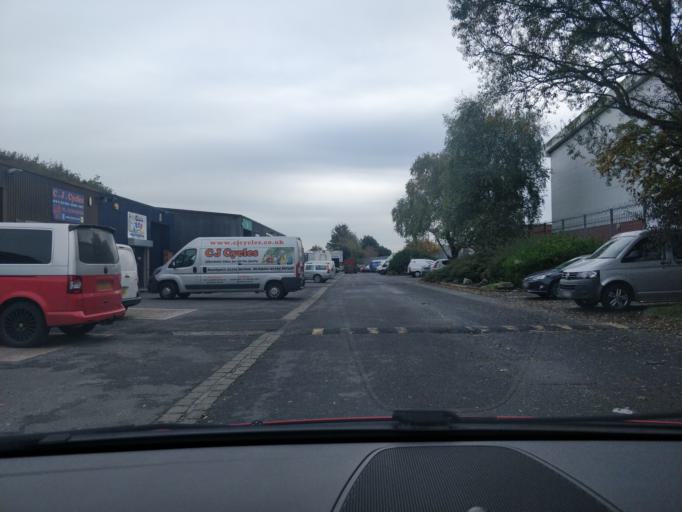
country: GB
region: England
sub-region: Sefton
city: Southport
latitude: 53.6449
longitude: -2.9943
